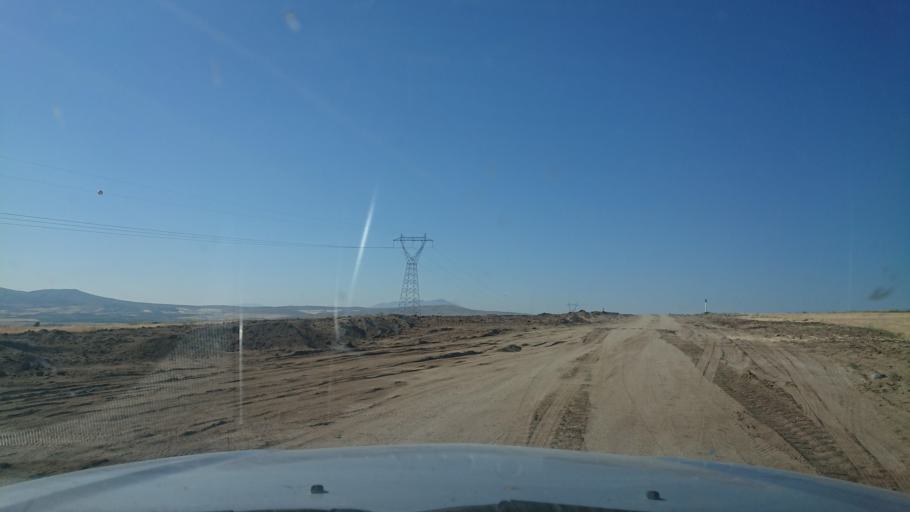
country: TR
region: Aksaray
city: Agacoren
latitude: 38.8423
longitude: 33.9441
